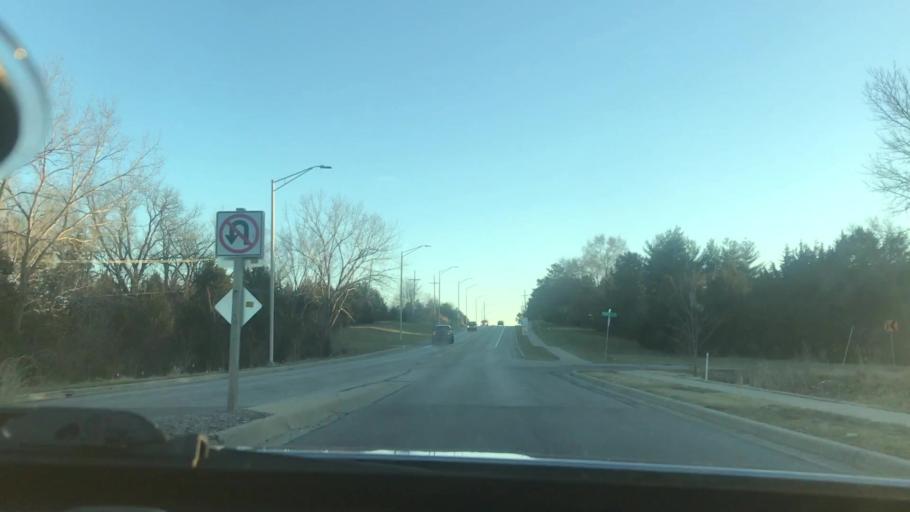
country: US
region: Kansas
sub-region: Johnson County
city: Olathe
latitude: 38.9402
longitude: -94.8162
